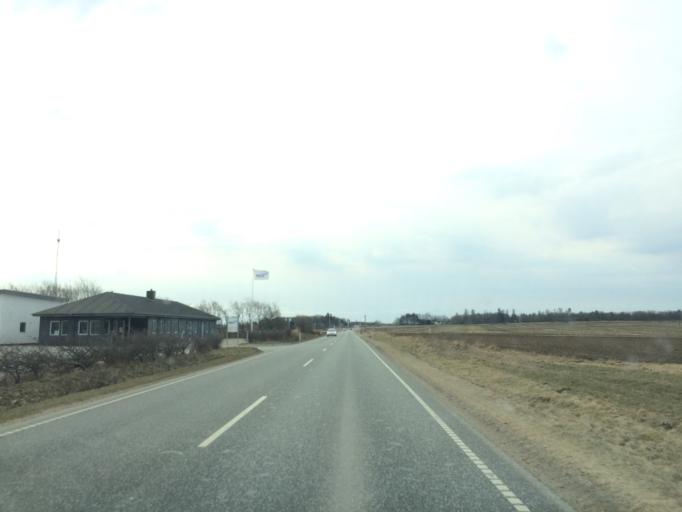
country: DK
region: Central Jutland
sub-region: Ringkobing-Skjern Kommune
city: Videbaek
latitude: 56.0921
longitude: 8.5075
